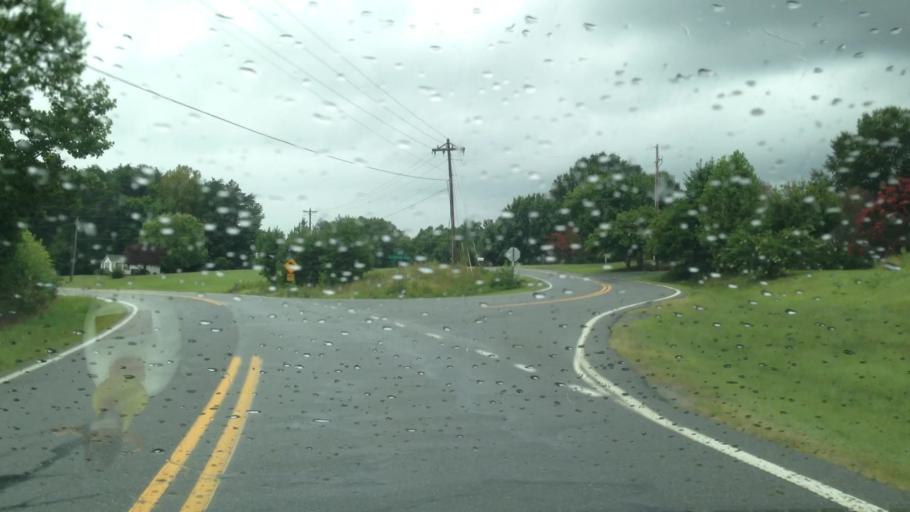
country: US
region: North Carolina
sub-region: Stokes County
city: Walnut Cove
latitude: 36.2633
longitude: -80.0988
